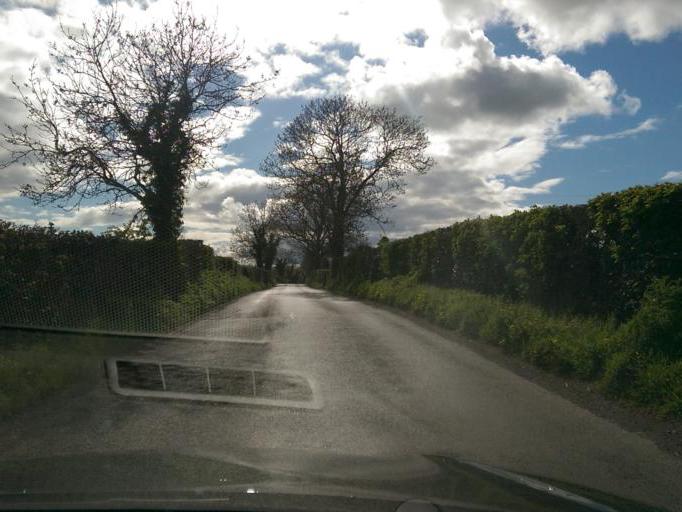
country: IE
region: Leinster
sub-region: Kildare
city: Kilcock
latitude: 53.5048
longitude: -6.6660
